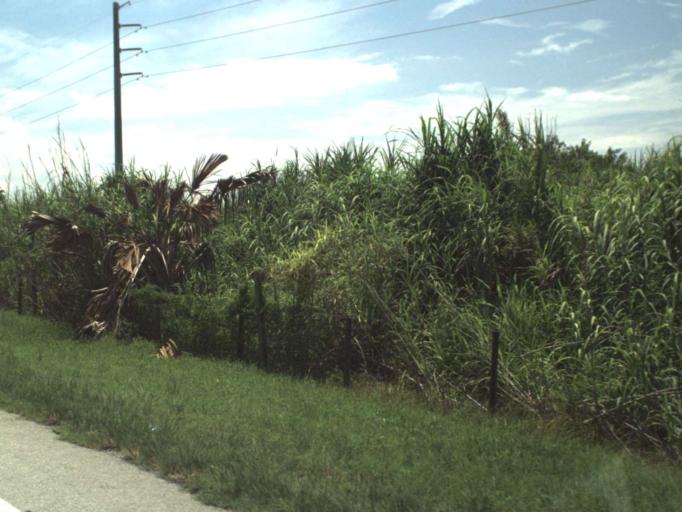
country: US
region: Florida
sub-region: Palm Beach County
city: Pahokee
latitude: 26.9370
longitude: -80.6107
